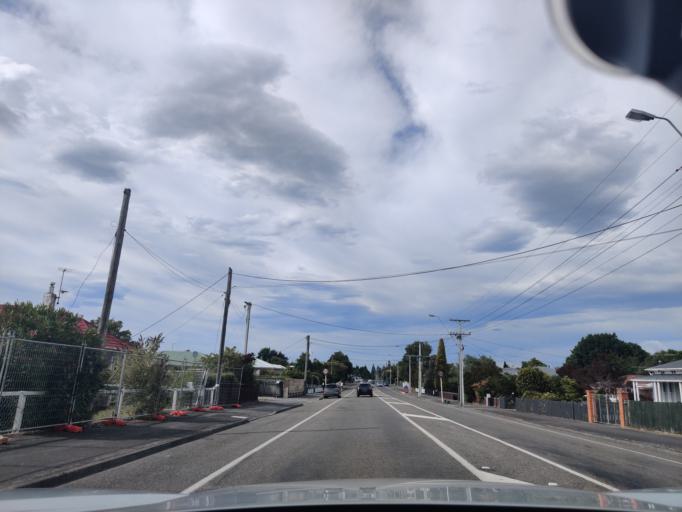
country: NZ
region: Wellington
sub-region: Masterton District
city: Masterton
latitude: -40.9403
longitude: 175.6702
